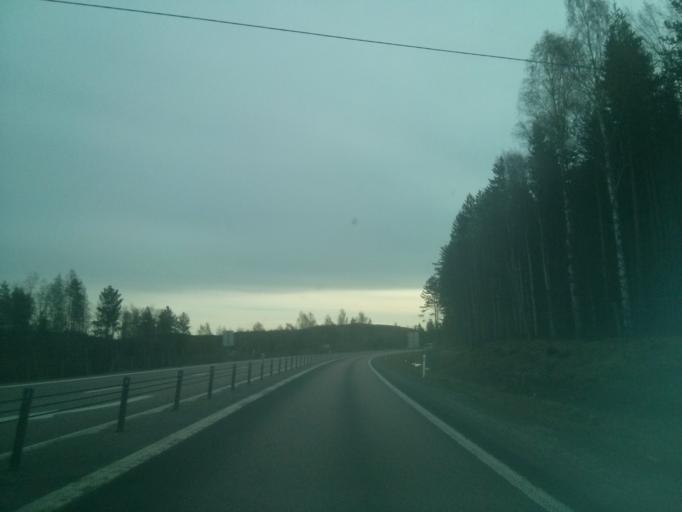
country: SE
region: Vaesternorrland
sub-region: Haernoesands Kommun
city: Haernoesand
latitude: 62.6118
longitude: 17.8427
